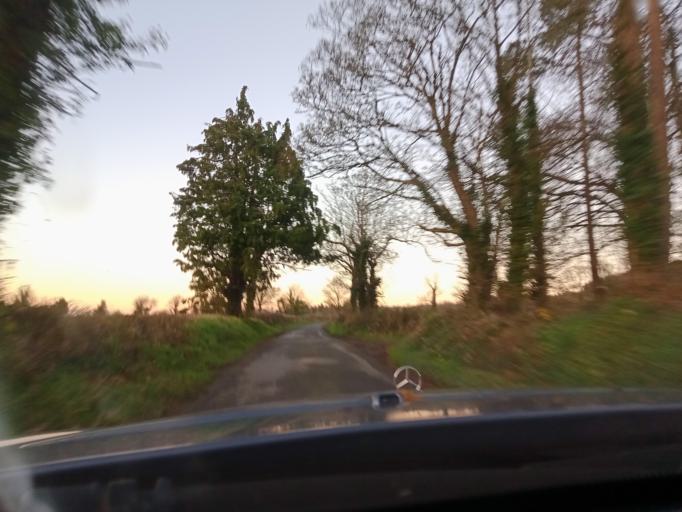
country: IE
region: Leinster
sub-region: Kilkenny
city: Thomastown
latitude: 52.4431
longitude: -7.1063
